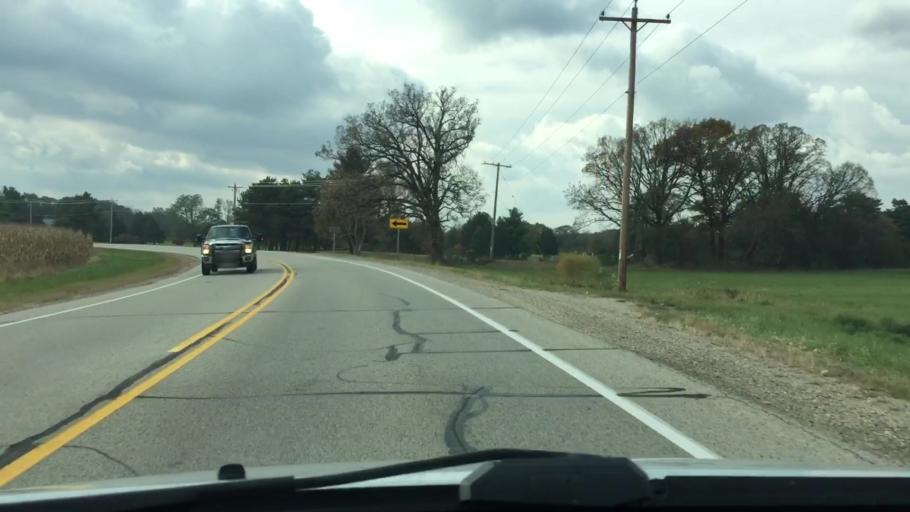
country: US
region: Wisconsin
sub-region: Waukesha County
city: Dousman
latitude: 42.9710
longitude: -88.4733
